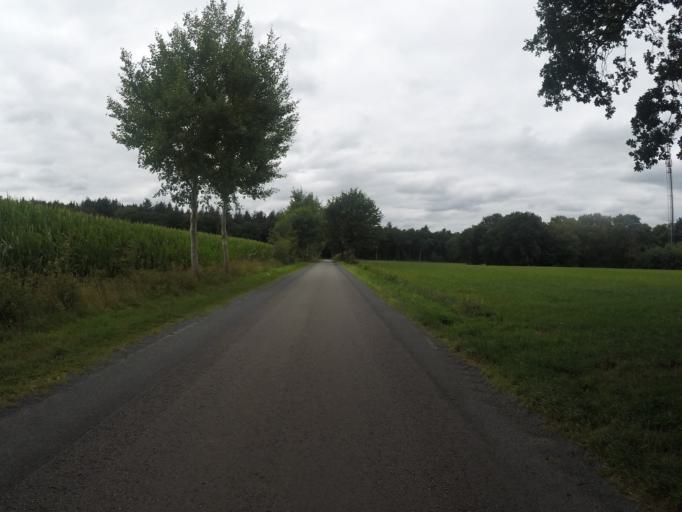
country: DE
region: Lower Saxony
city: Himmelpforten
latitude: 53.6078
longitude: 9.3275
